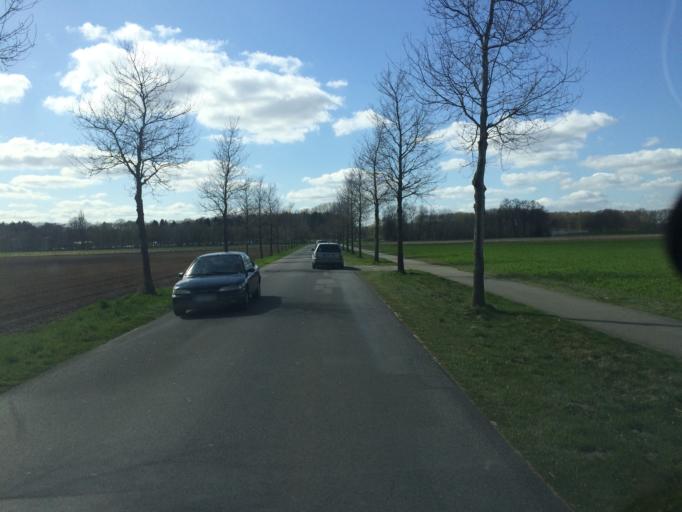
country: DE
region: Lower Saxony
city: Haren
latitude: 52.7974
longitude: 7.2127
